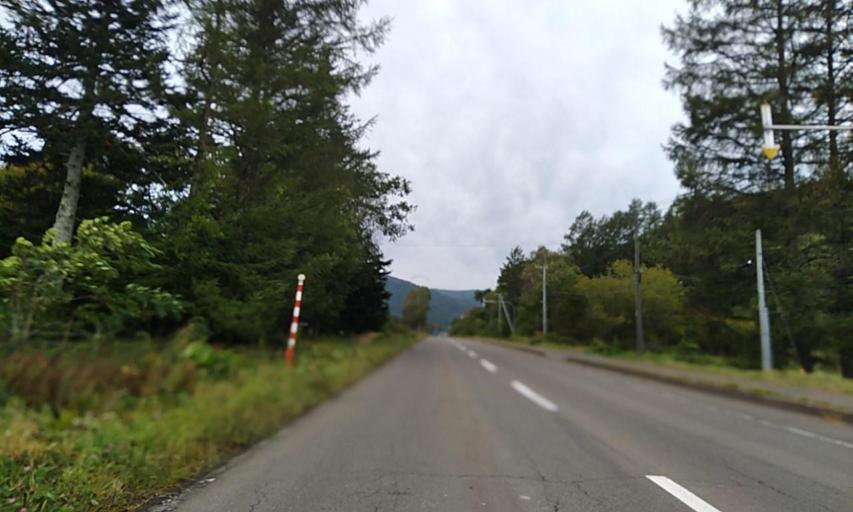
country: JP
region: Hokkaido
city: Bihoro
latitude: 43.5550
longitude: 144.3506
